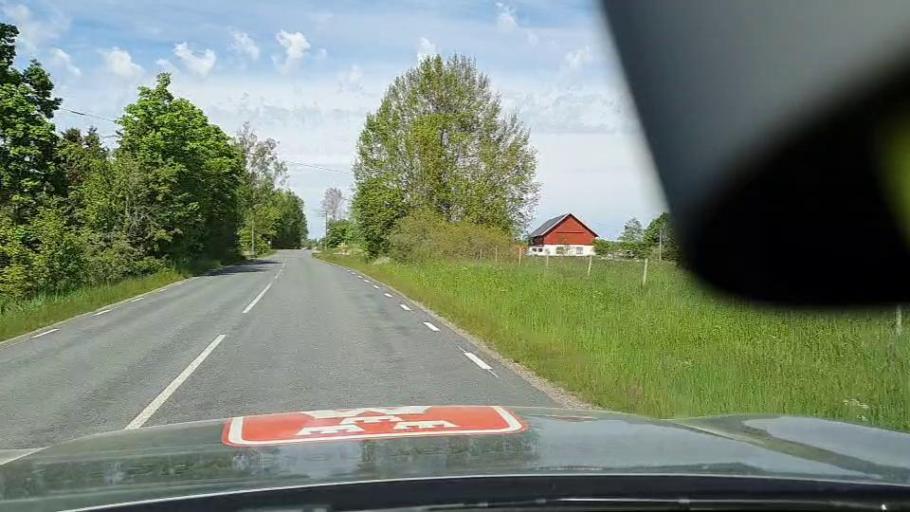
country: SE
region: Soedermanland
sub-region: Eskilstuna Kommun
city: Skogstorp
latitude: 59.3067
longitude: 16.4629
